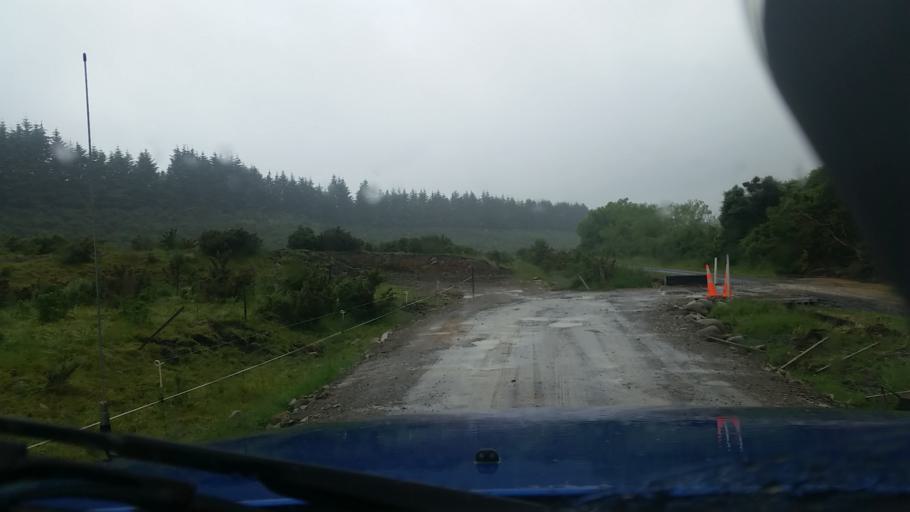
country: NZ
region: Canterbury
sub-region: Ashburton District
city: Methven
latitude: -43.5762
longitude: 171.5259
